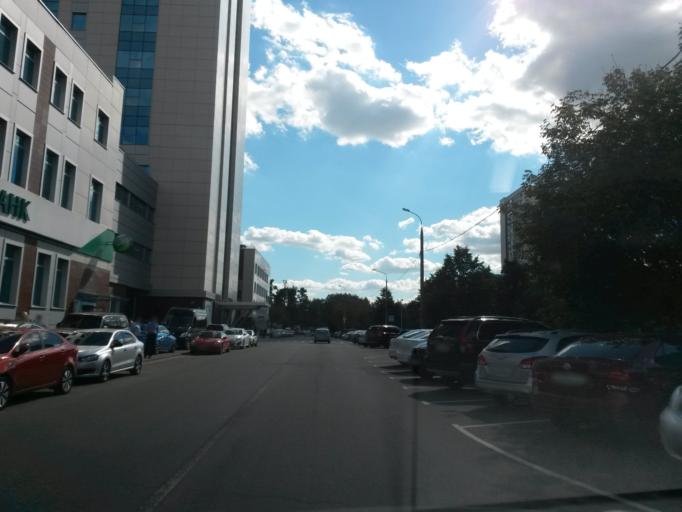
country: RU
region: Moskovskaya
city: Kozhukhovo
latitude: 55.7026
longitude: 37.6888
